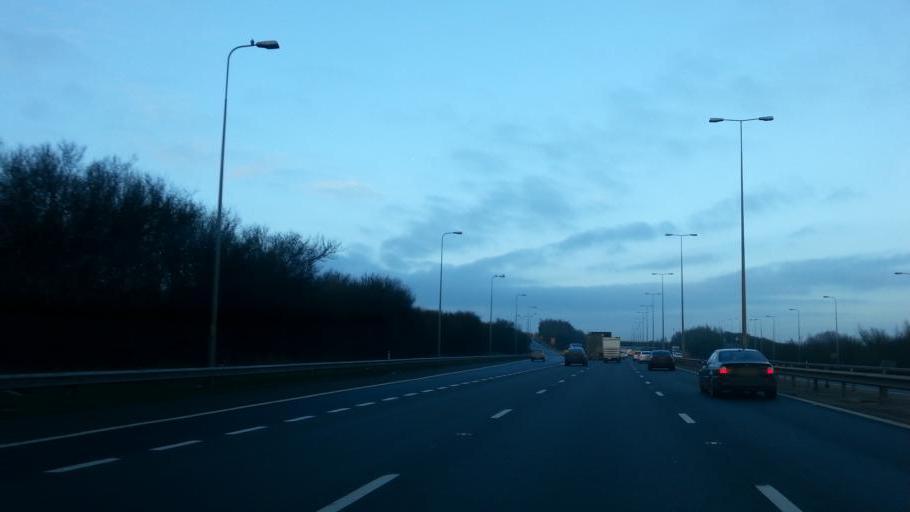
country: GB
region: England
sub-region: Worcestershire
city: Kempsey
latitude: 52.1639
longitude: -2.1847
